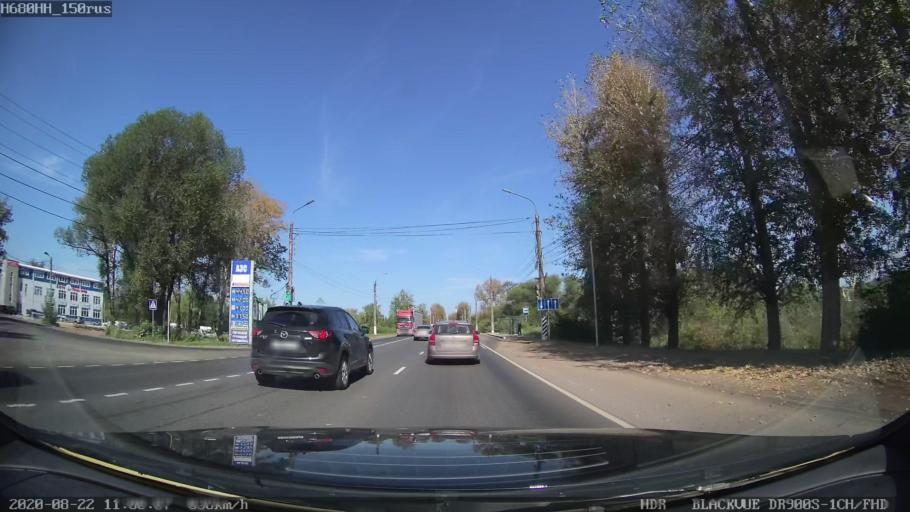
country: RU
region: Tverskaya
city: Tver
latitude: 56.8251
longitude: 35.9738
